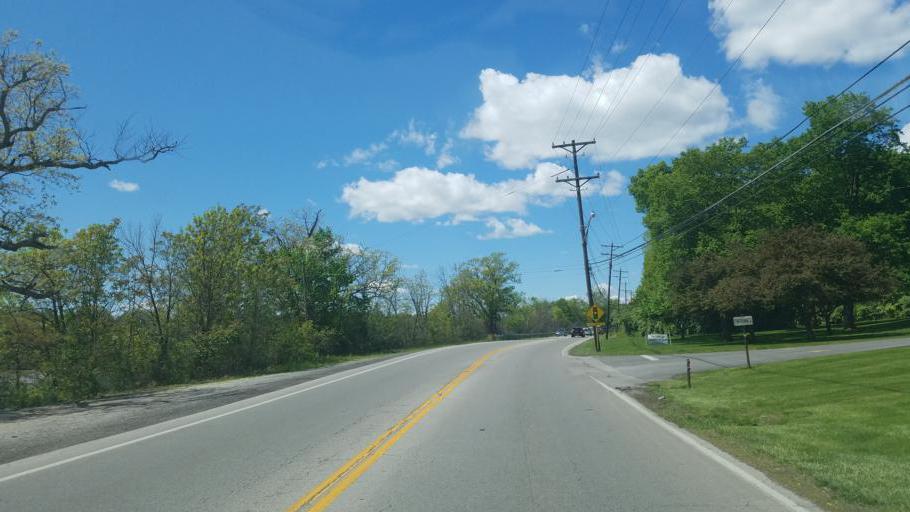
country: US
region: Ohio
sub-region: Franklin County
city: Dublin
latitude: 40.0589
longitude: -83.1011
